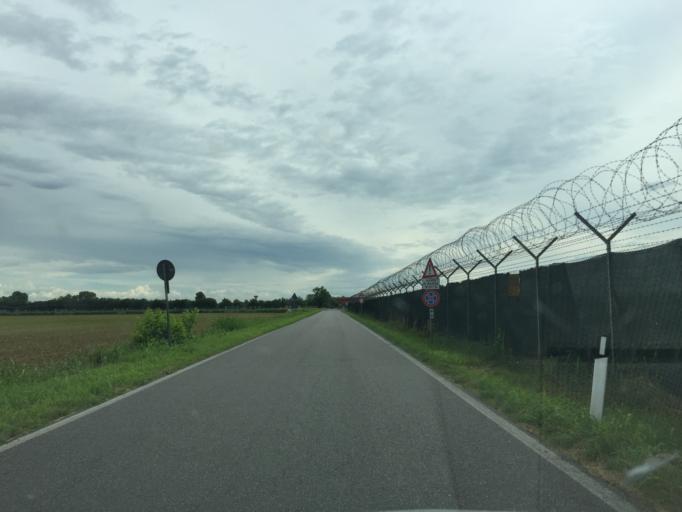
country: IT
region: Lombardy
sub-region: Provincia di Brescia
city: Ghedi
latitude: 45.4234
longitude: 10.2836
